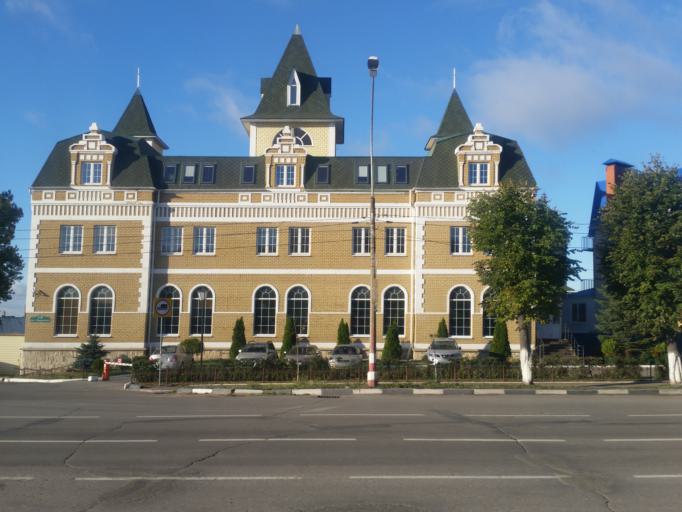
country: RU
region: Ulyanovsk
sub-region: Ulyanovskiy Rayon
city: Ulyanovsk
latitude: 54.3351
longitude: 48.3838
